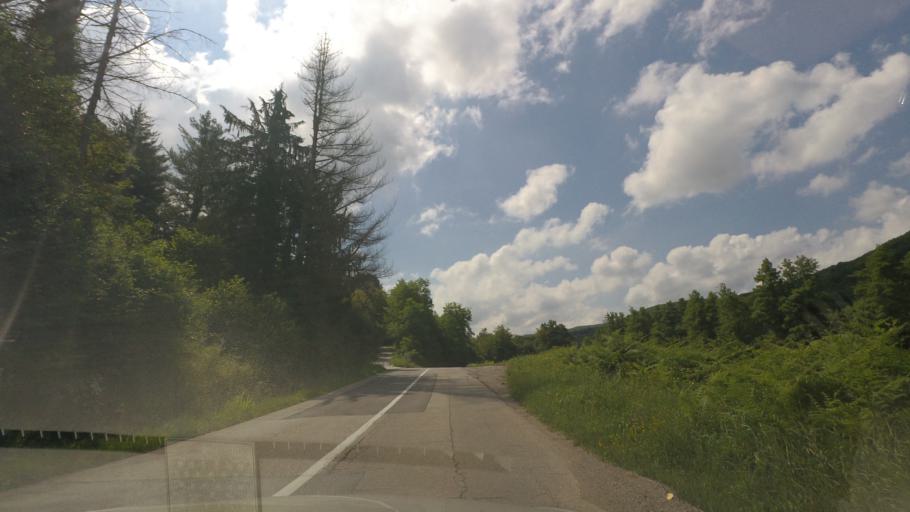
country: HR
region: Karlovacka
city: Vojnic
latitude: 45.3753
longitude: 15.6514
